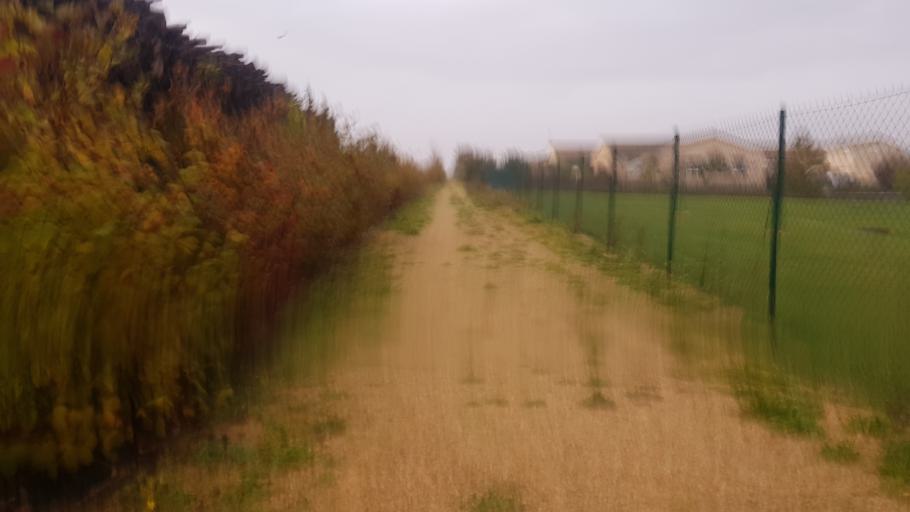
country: FR
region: Poitou-Charentes
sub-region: Departement de la Vienne
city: Chasseneuil-du-Poitou
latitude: 46.6580
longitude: 0.3418
